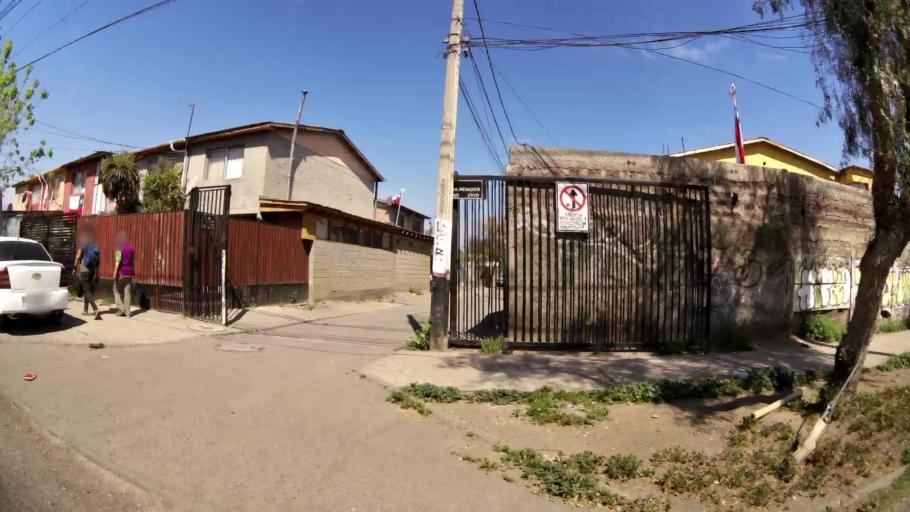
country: CL
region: Santiago Metropolitan
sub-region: Provincia de Cordillera
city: Puente Alto
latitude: -33.6208
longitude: -70.6102
